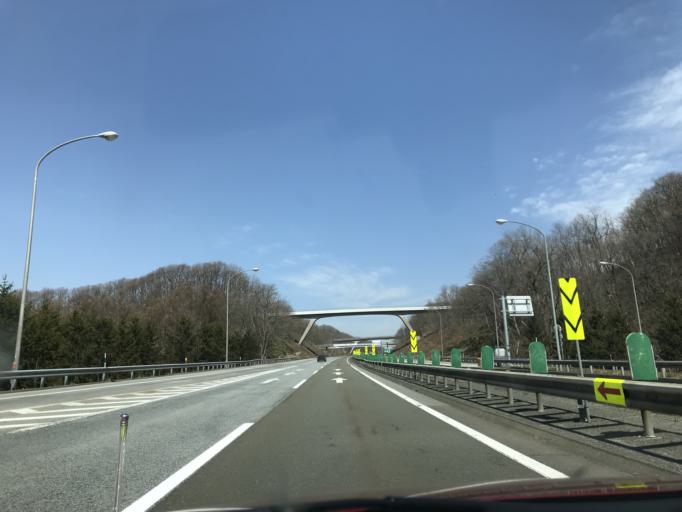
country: JP
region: Hokkaido
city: Iwamizawa
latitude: 43.2453
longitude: 141.8303
